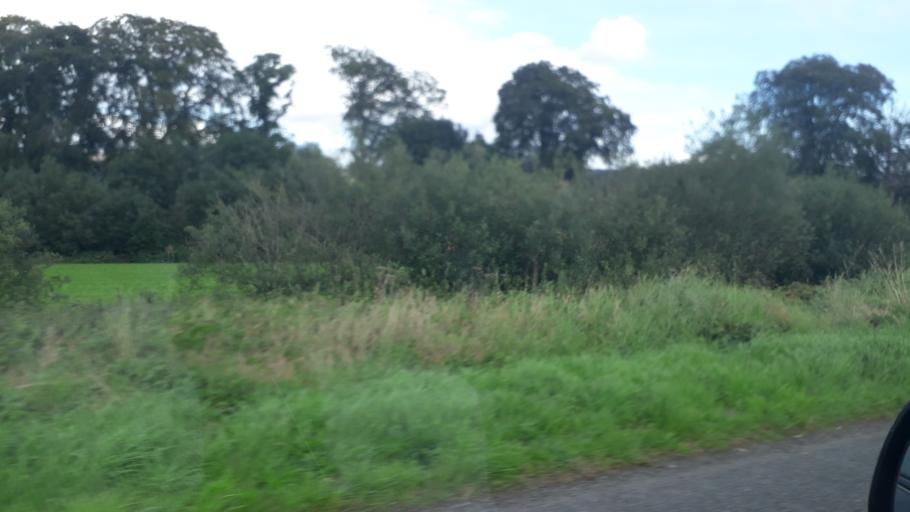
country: IE
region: Leinster
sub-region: Lu
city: Blackrock
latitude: 54.0275
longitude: -6.3485
